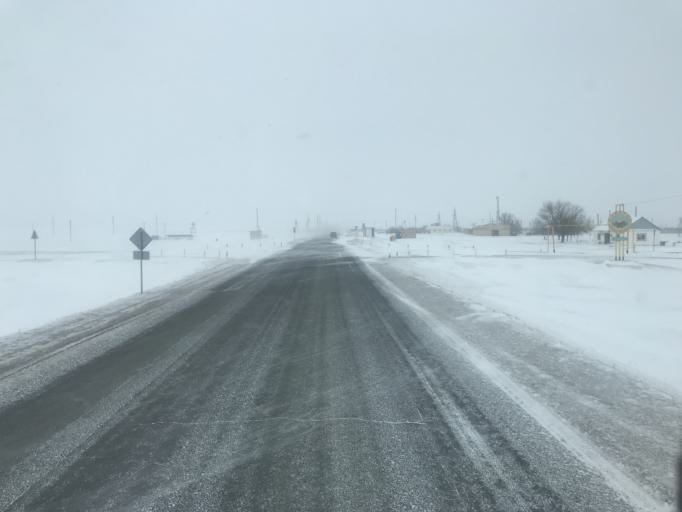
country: KZ
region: Batys Qazaqstan
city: Chapaev
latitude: 50.5130
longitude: 51.0577
